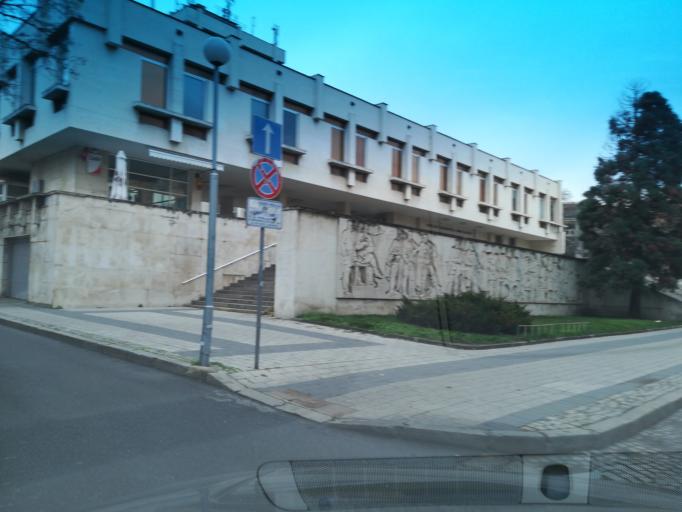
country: BG
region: Plovdiv
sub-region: Obshtina Plovdiv
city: Plovdiv
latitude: 42.1394
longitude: 24.7454
